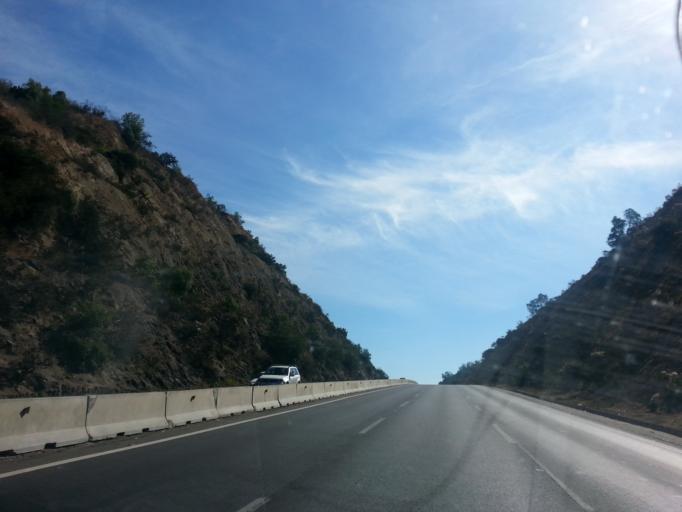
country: CL
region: Valparaiso
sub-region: Provincia de Marga Marga
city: Quilpue
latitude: -33.2868
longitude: -71.4252
